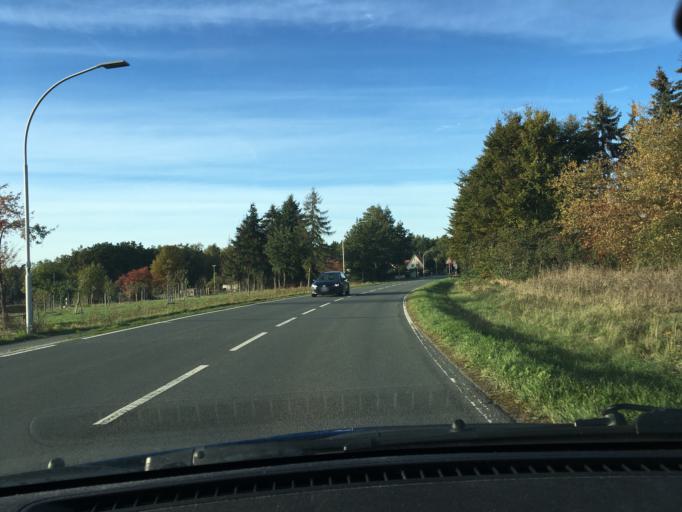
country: DE
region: Lower Saxony
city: Fassberg
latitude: 52.9310
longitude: 10.1356
